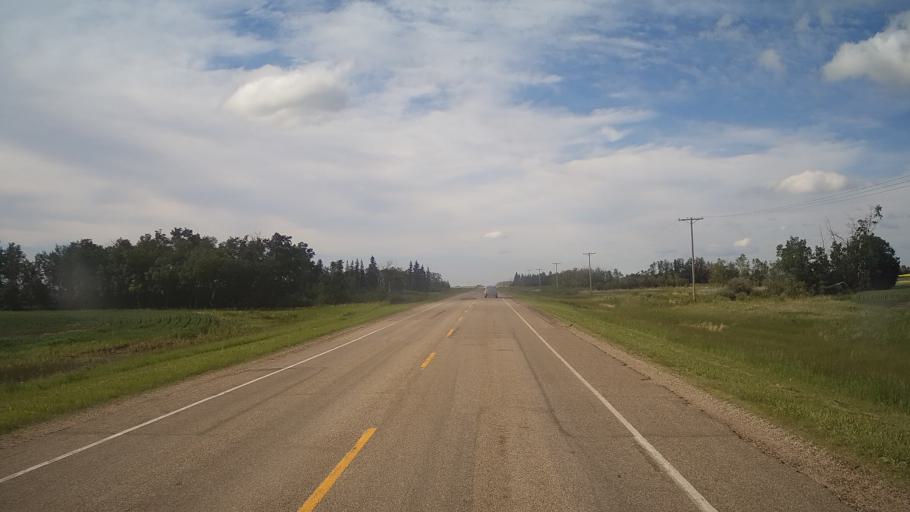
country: CA
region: Saskatchewan
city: Foam Lake
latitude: 51.5984
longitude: -103.8459
